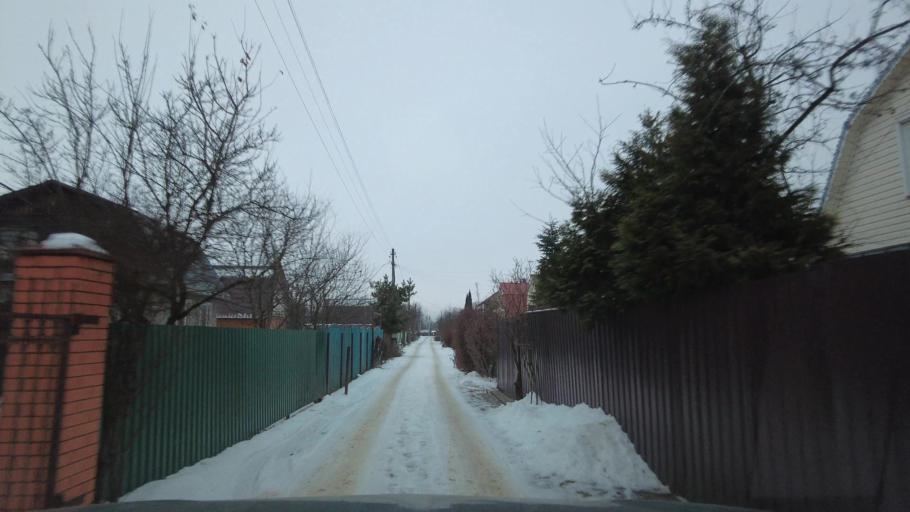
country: RU
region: Moskovskaya
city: Novopodrezkovo
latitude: 55.9847
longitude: 37.3920
